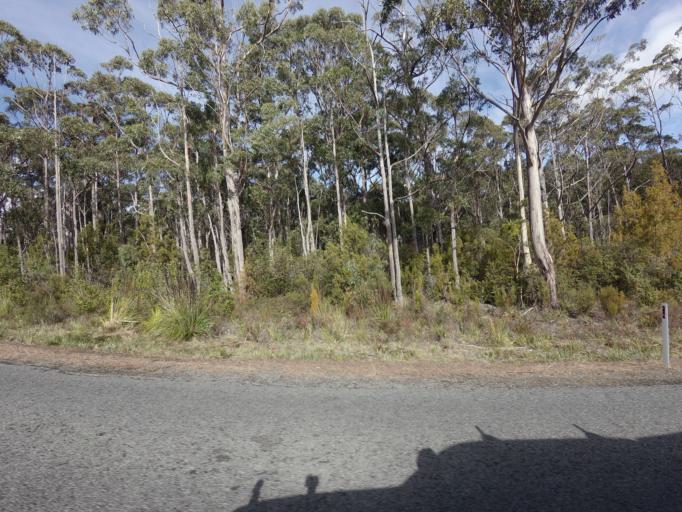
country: AU
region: Tasmania
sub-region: Clarence
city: Sandford
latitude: -43.1250
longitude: 147.7697
